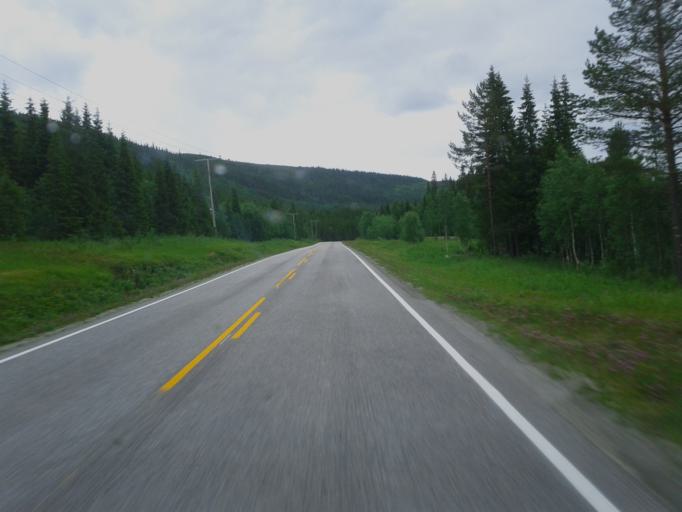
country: NO
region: Nord-Trondelag
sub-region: Namsskogan
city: Namsskogan
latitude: 64.8768
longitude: 13.0672
